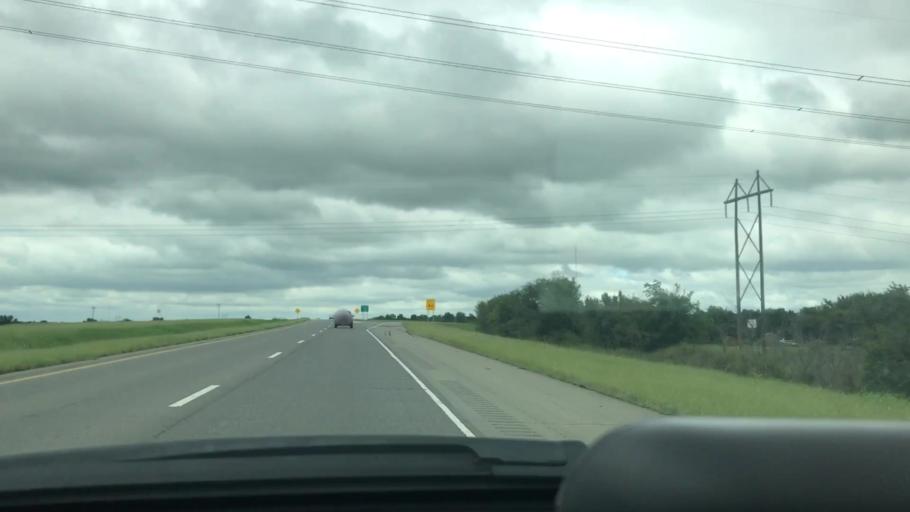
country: US
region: Oklahoma
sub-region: McIntosh County
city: Checotah
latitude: 35.5718
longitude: -95.4909
